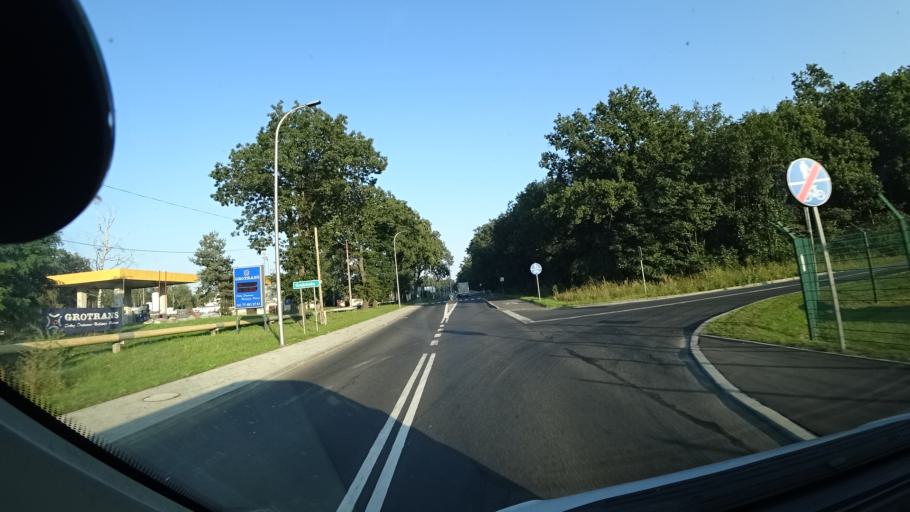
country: PL
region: Opole Voivodeship
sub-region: Powiat kedzierzynsko-kozielski
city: Bierawa
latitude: 50.2873
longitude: 18.2774
